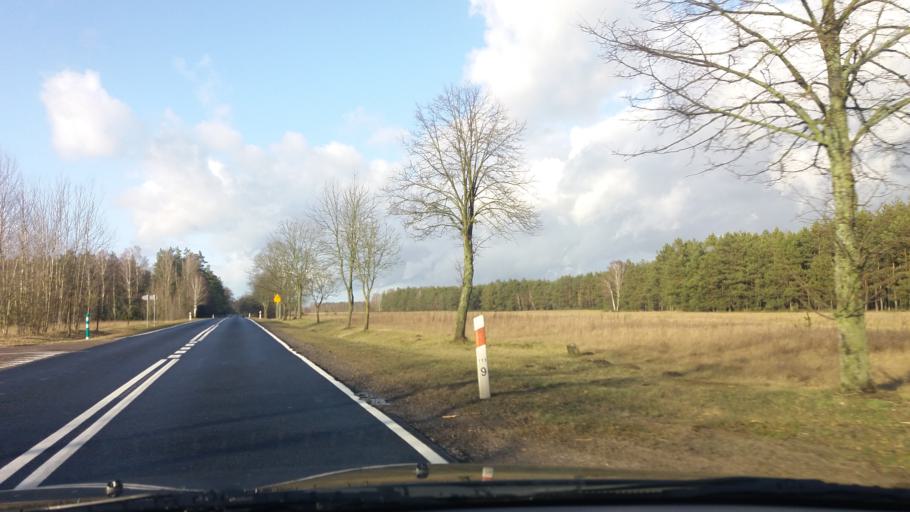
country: PL
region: Masovian Voivodeship
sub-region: Powiat przasnyski
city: Chorzele
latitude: 53.3273
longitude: 20.9047
